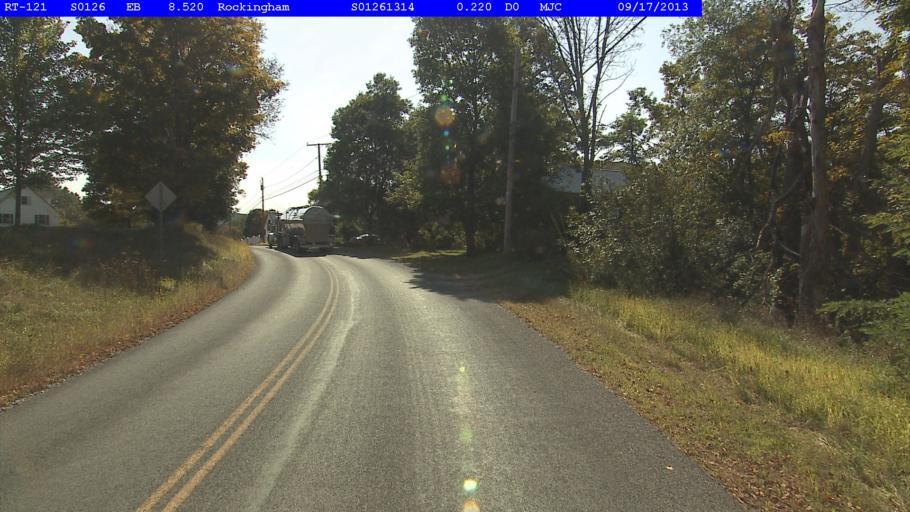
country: US
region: Vermont
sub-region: Windham County
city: Rockingham
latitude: 43.1498
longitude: -72.5542
